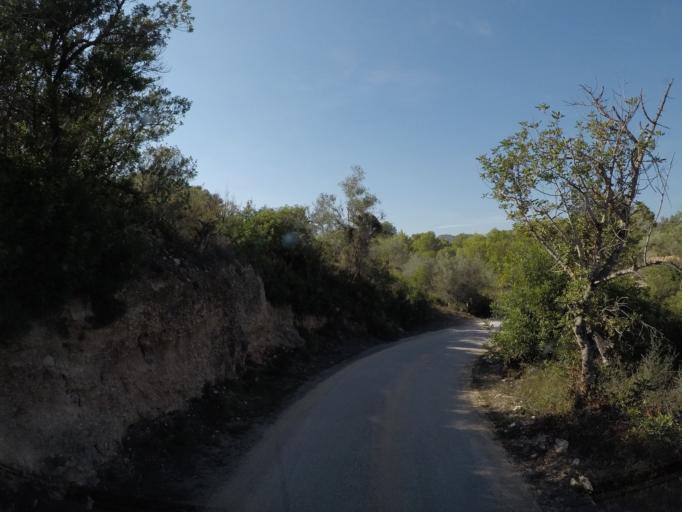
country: ES
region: Catalonia
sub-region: Provincia de Tarragona
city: El Perello
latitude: 40.9046
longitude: 0.7265
